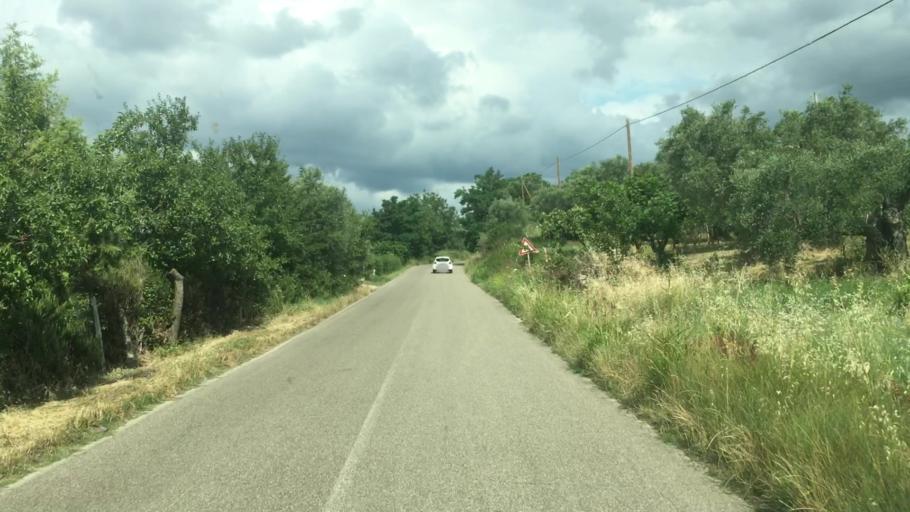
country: IT
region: Basilicate
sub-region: Provincia di Matera
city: San Mauro Forte
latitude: 40.4798
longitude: 16.2645
